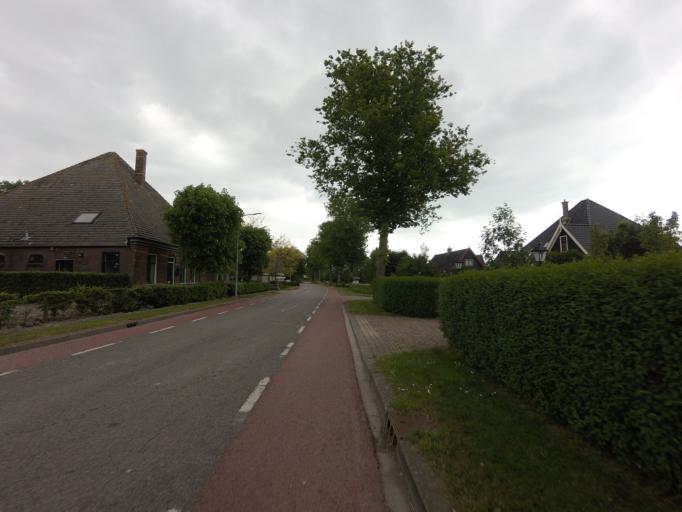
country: NL
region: North Holland
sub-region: Gemeente Hoorn
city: Hoorn
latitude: 52.6202
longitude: 4.9992
